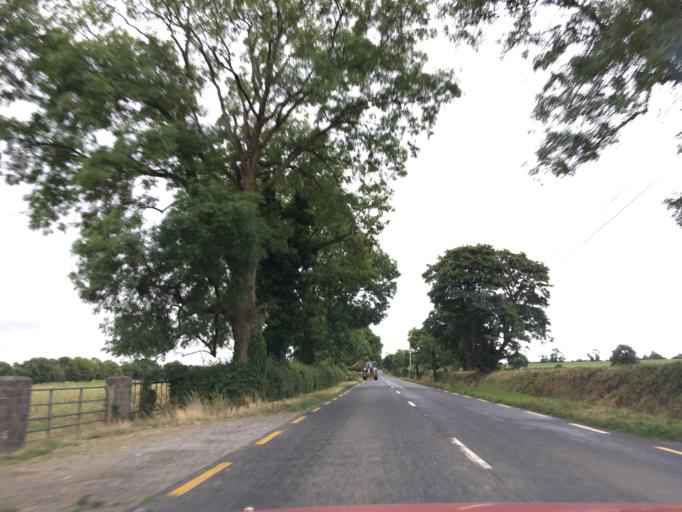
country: IE
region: Munster
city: Fethard
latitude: 52.4354
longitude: -7.7898
